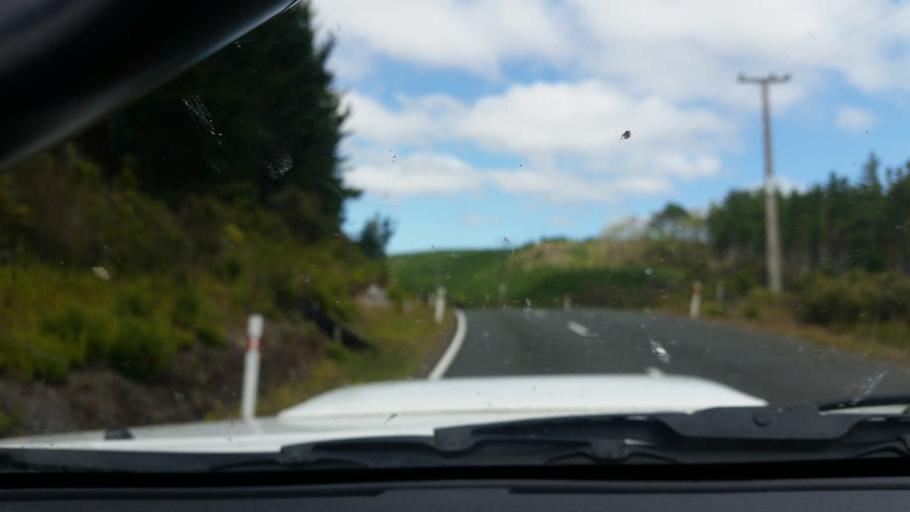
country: NZ
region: Northland
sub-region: Kaipara District
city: Dargaville
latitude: -35.8165
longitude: 173.7162
